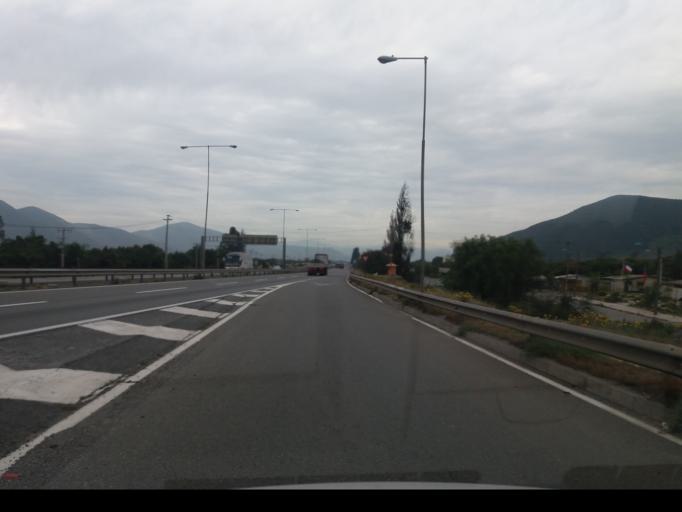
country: CL
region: Valparaiso
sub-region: Provincia de Quillota
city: Hacienda La Calera
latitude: -32.8409
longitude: -71.1102
